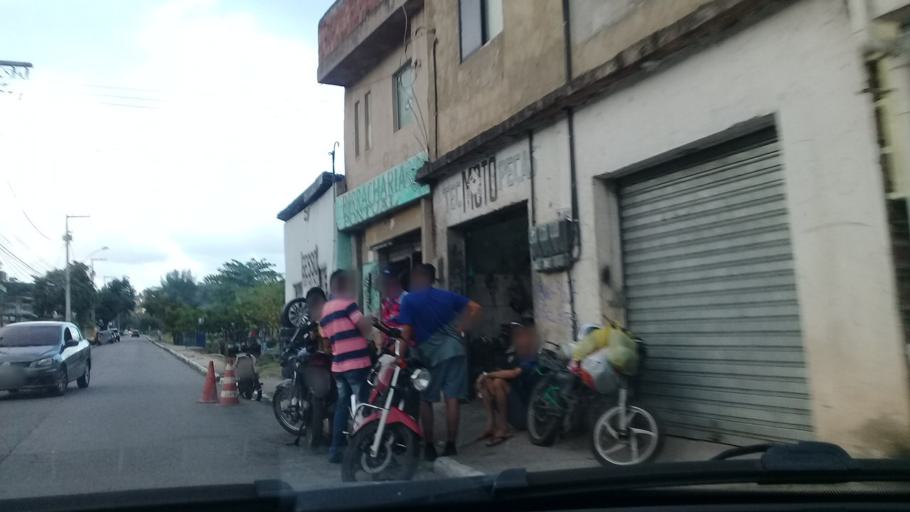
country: BR
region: Pernambuco
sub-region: Jaboatao Dos Guararapes
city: Jaboatao dos Guararapes
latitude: -8.1266
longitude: -34.9502
